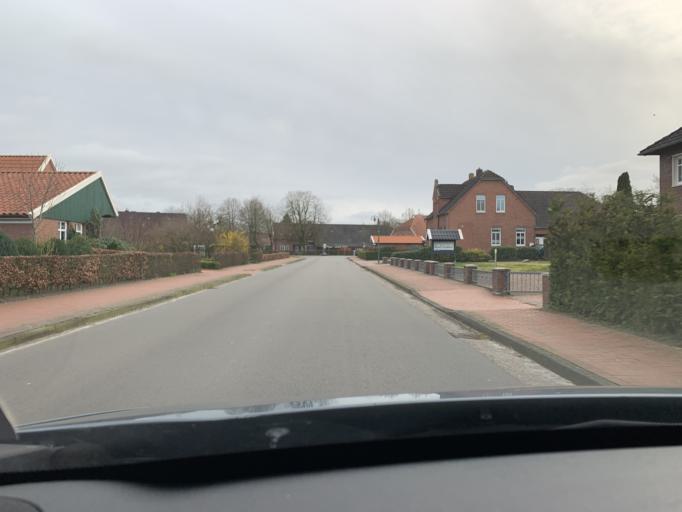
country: DE
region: Lower Saxony
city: Detern
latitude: 53.2556
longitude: 7.7107
